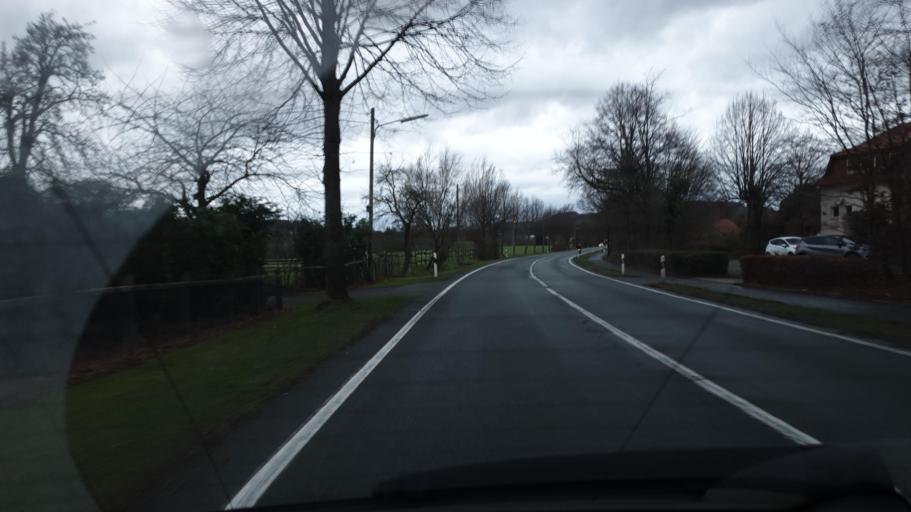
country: DE
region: North Rhine-Westphalia
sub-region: Regierungsbezirk Detmold
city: Vlotho
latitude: 52.1283
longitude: 8.8372
